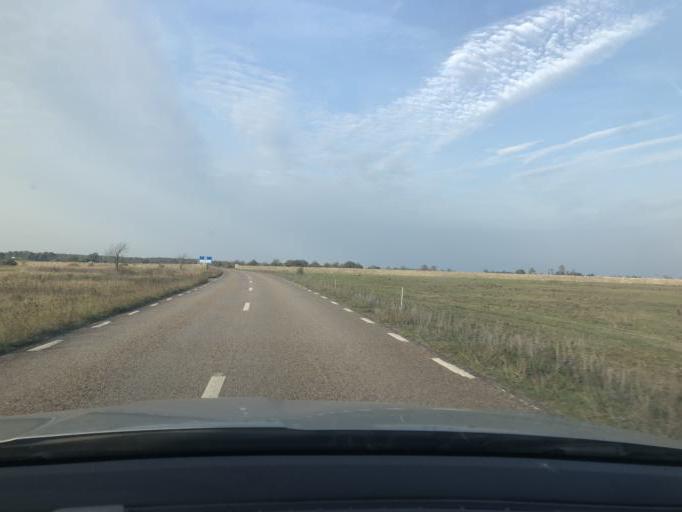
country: SE
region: Kalmar
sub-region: Morbylanga Kommun
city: Moerbylanga
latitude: 56.2479
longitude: 16.4174
